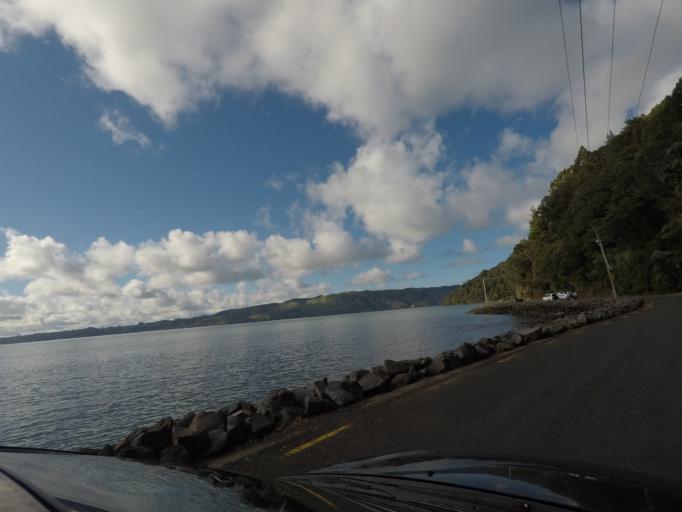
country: NZ
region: Auckland
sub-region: Auckland
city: Titirangi
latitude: -37.0107
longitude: 174.5624
